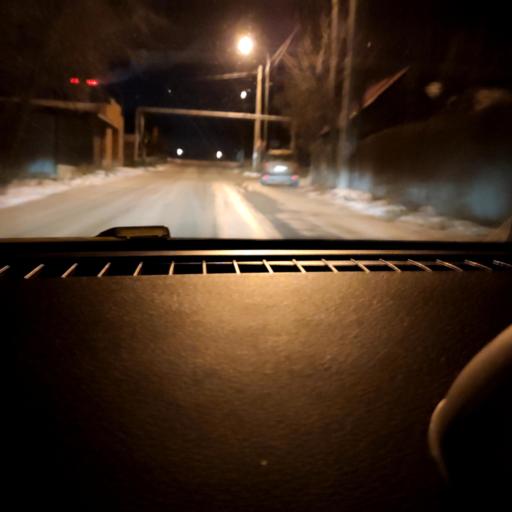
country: RU
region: Samara
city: Petra-Dubrava
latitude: 53.2867
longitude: 50.2427
